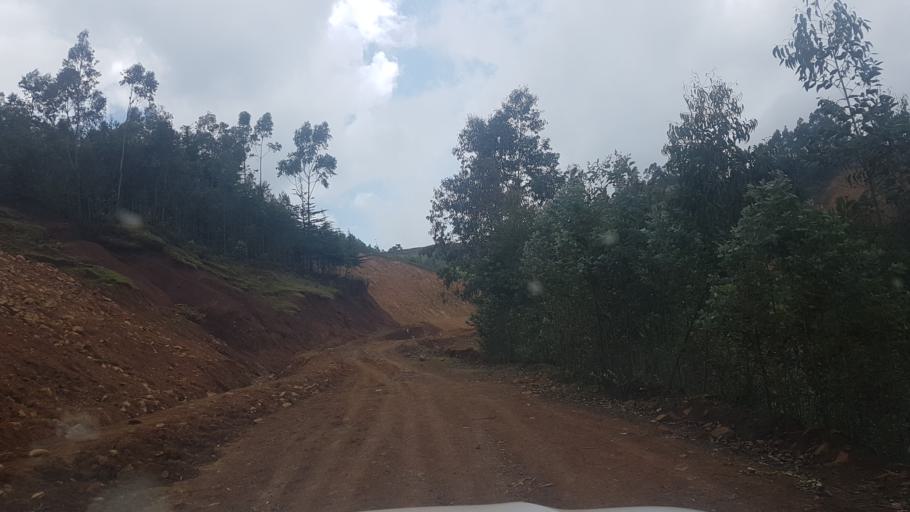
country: ET
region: Southern Nations, Nationalities, and People's Region
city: Arba Minch'
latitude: 6.3229
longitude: 37.5487
